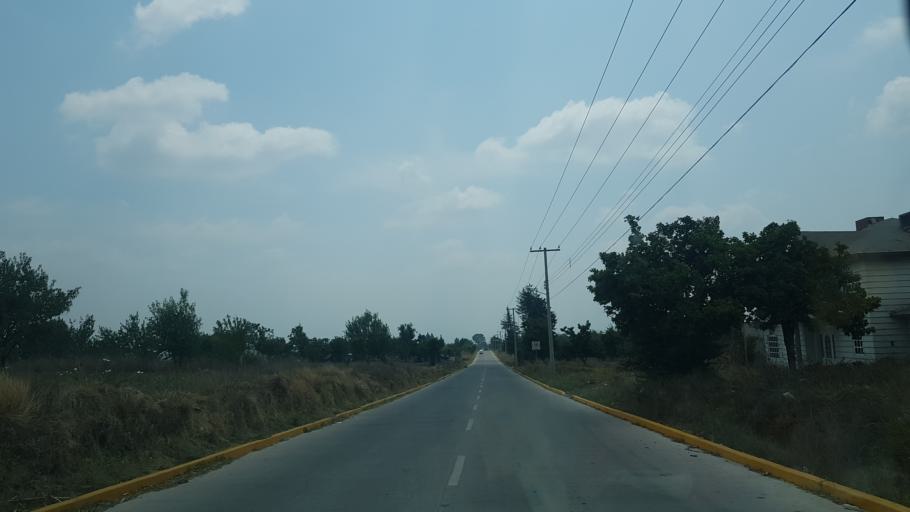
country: MX
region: Puebla
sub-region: Huejotzingo
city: San Juan Pancoac
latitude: 19.1385
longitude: -98.4356
